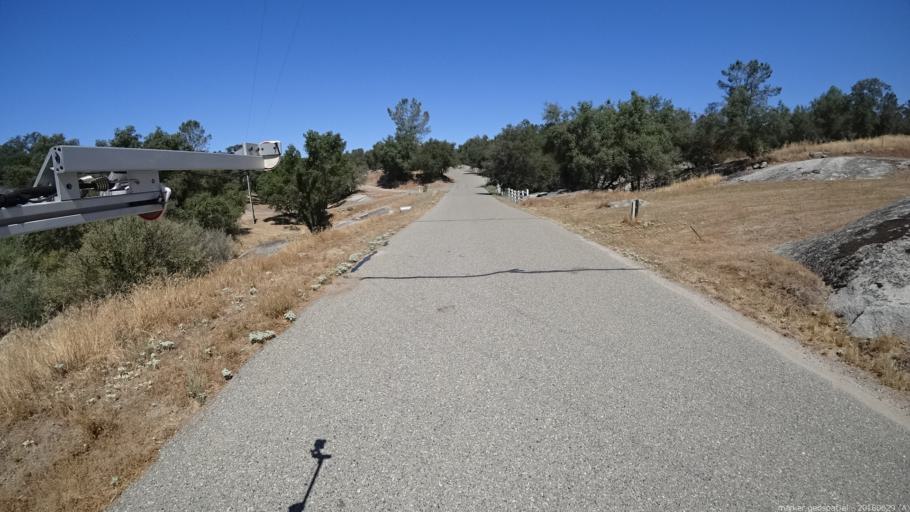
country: US
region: California
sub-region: Madera County
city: Yosemite Lakes
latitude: 37.1613
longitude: -119.7553
